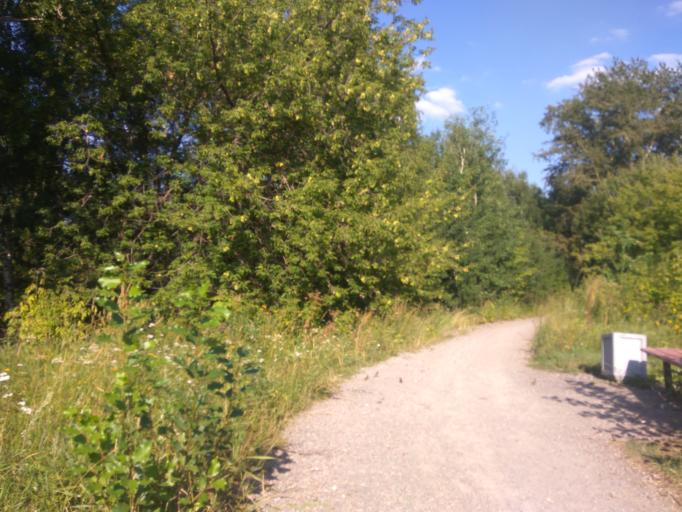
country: RU
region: Moscow
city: Shchukino
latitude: 55.8074
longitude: 37.4345
